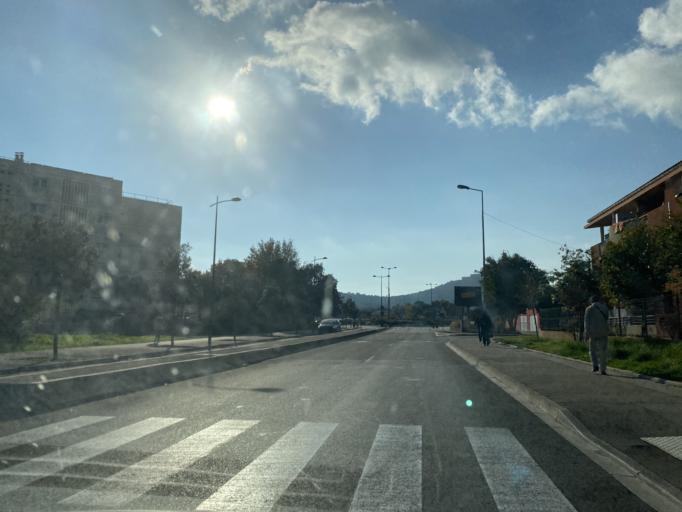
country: FR
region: Provence-Alpes-Cote d'Azur
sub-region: Departement du Var
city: Six-Fours-les-Plages
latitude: 43.1110
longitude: 5.8613
